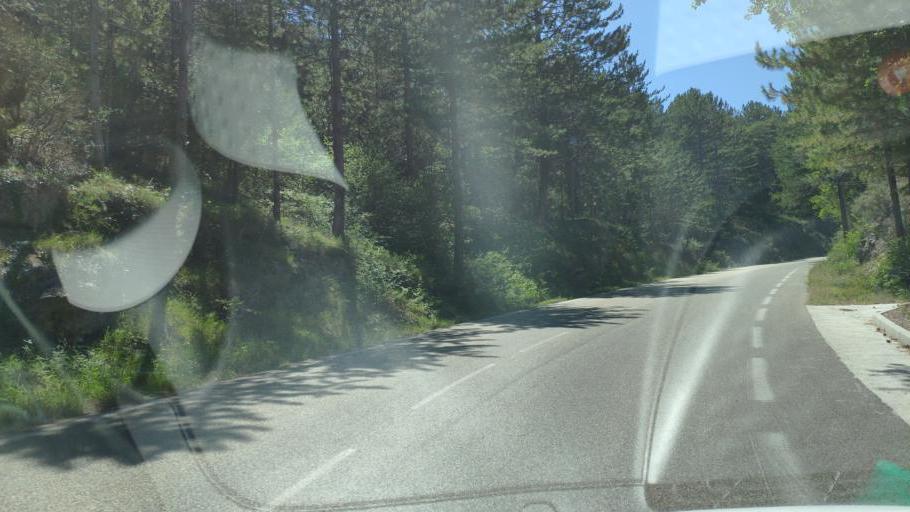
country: FR
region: Provence-Alpes-Cote d'Azur
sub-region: Departement du Vaucluse
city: Malaucene
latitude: 44.1656
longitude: 5.1473
